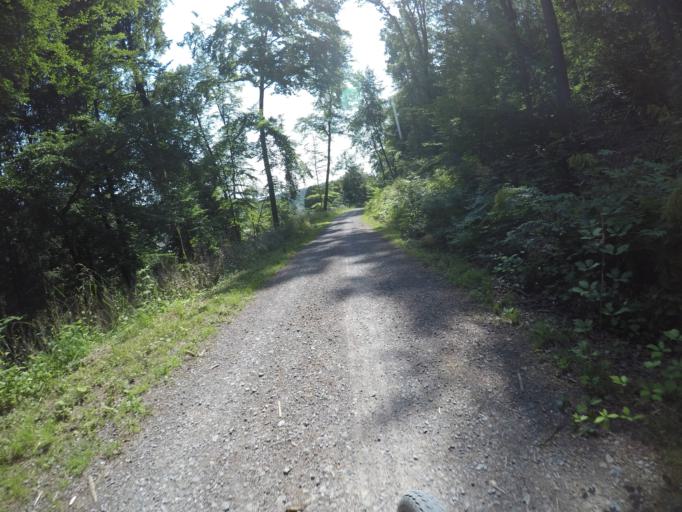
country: DE
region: Baden-Wuerttemberg
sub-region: Regierungsbezirk Stuttgart
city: Schlaitdorf
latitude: 48.6231
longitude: 9.1997
